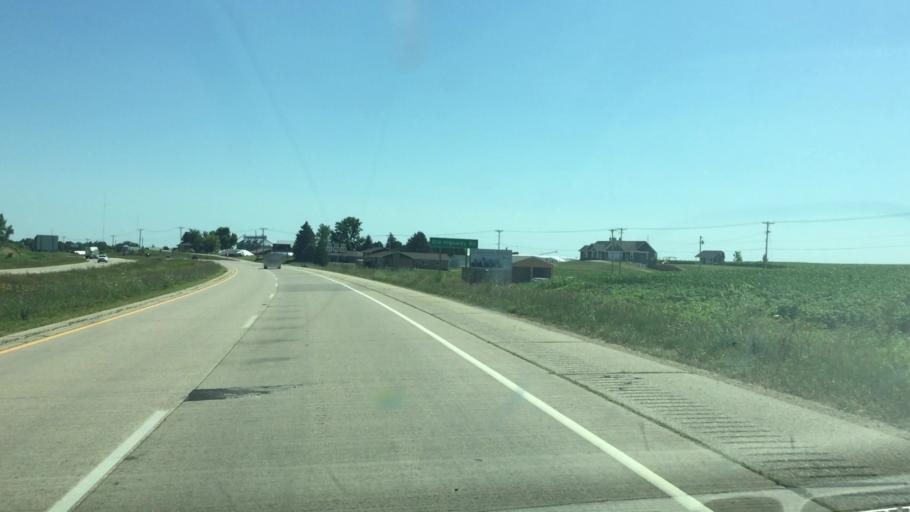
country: US
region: Wisconsin
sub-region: Grant County
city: Dickeyville
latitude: 42.5728
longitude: -90.6118
